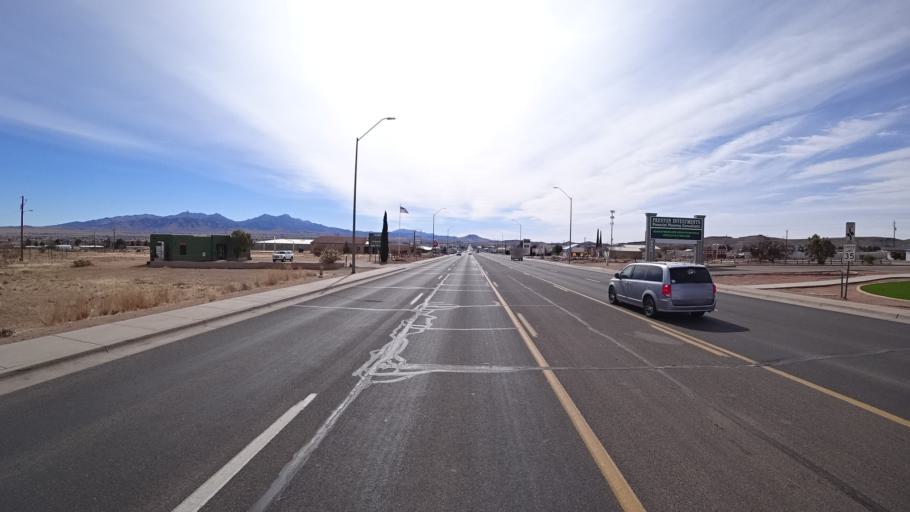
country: US
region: Arizona
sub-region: Mohave County
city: New Kingman-Butler
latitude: 35.2501
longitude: -114.0389
